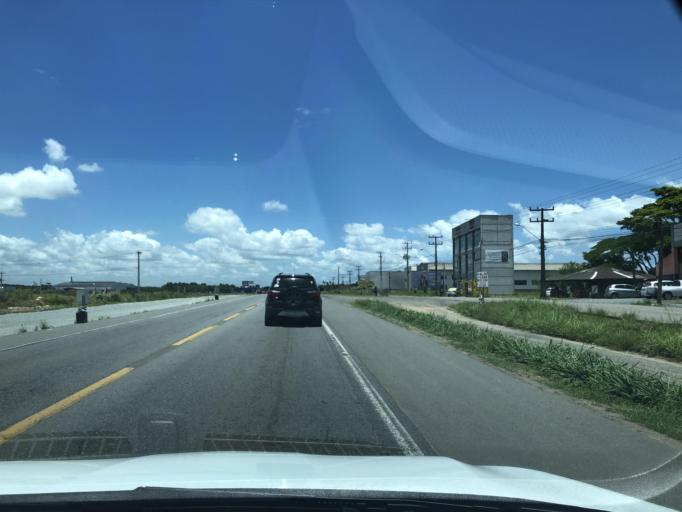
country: BR
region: Santa Catarina
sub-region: Joinville
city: Joinville
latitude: -26.3853
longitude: -48.7294
